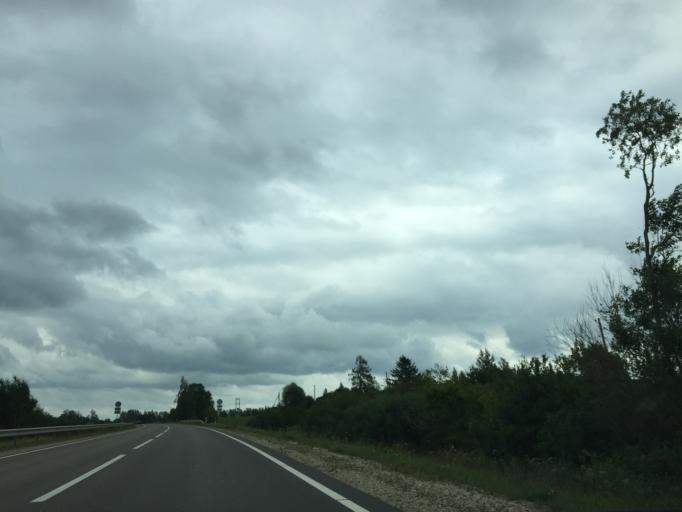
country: LV
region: Rezekne
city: Rezekne
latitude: 56.5308
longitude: 27.2668
